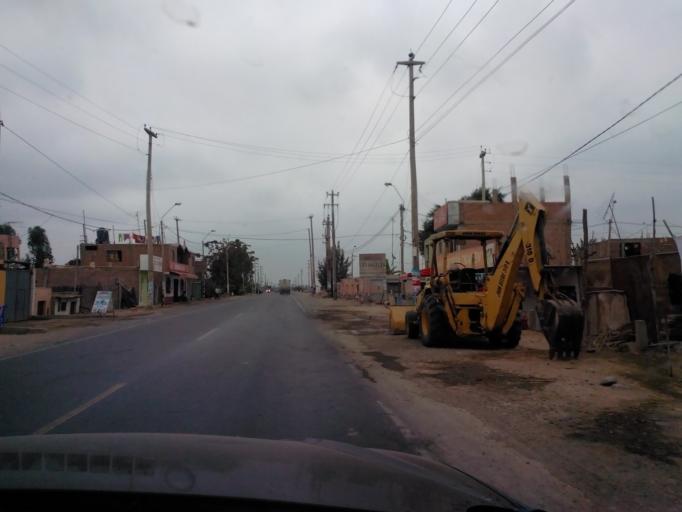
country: PE
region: Ica
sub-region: Provincia de Chincha
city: Chincha Baja
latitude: -13.5242
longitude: -76.1389
